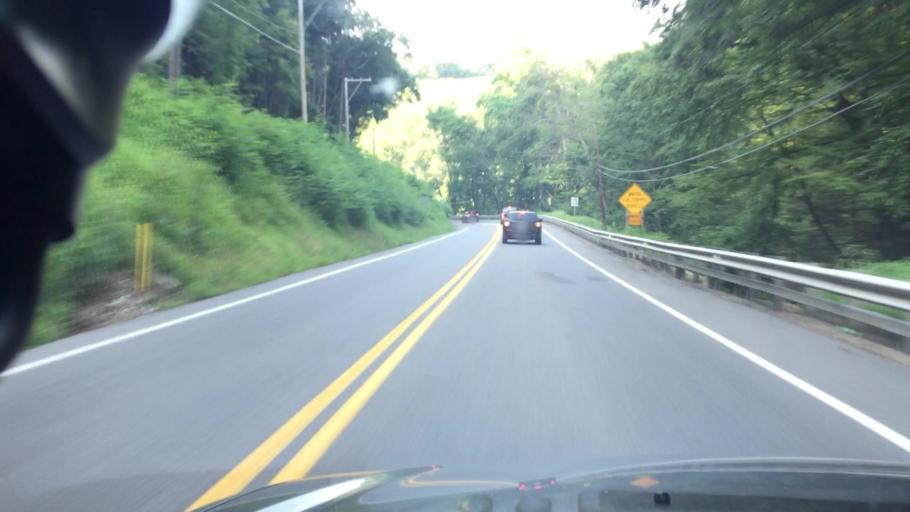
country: US
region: Pennsylvania
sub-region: Columbia County
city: Catawissa
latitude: 40.9381
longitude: -76.4564
